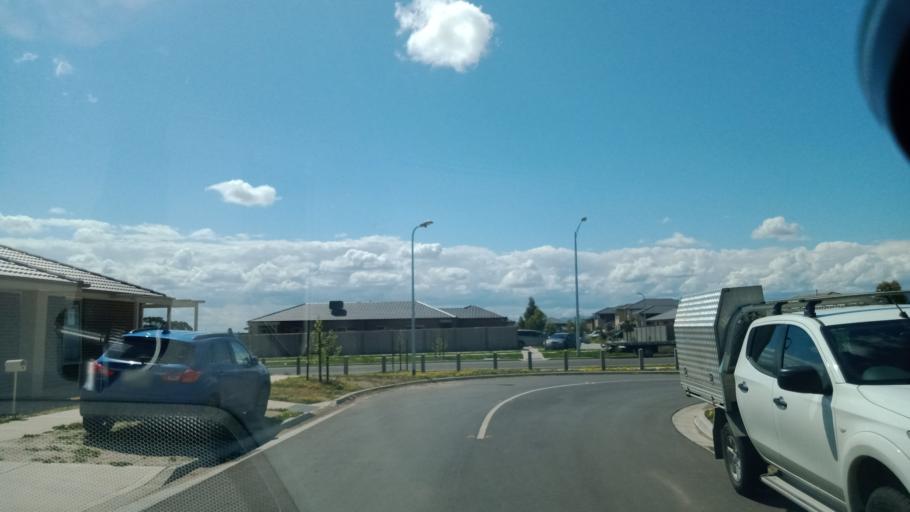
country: AU
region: Victoria
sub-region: Casey
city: Cranbourne West
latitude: -38.1013
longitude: 145.2449
